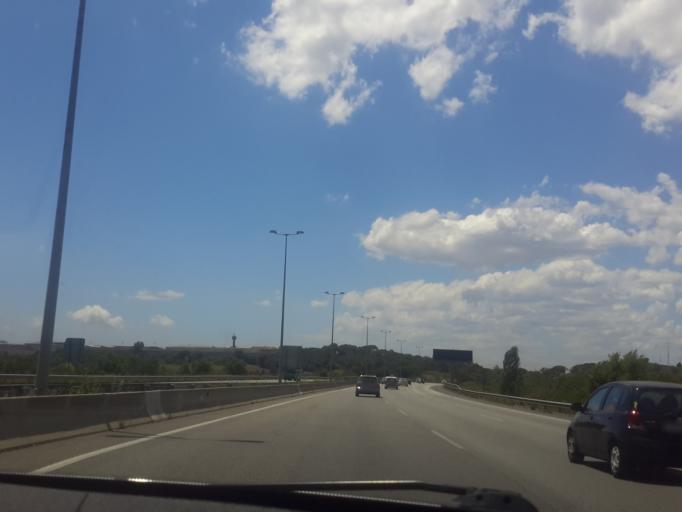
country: ES
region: Catalonia
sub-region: Provincia de Barcelona
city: Granollers
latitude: 41.5860
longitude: 2.3012
